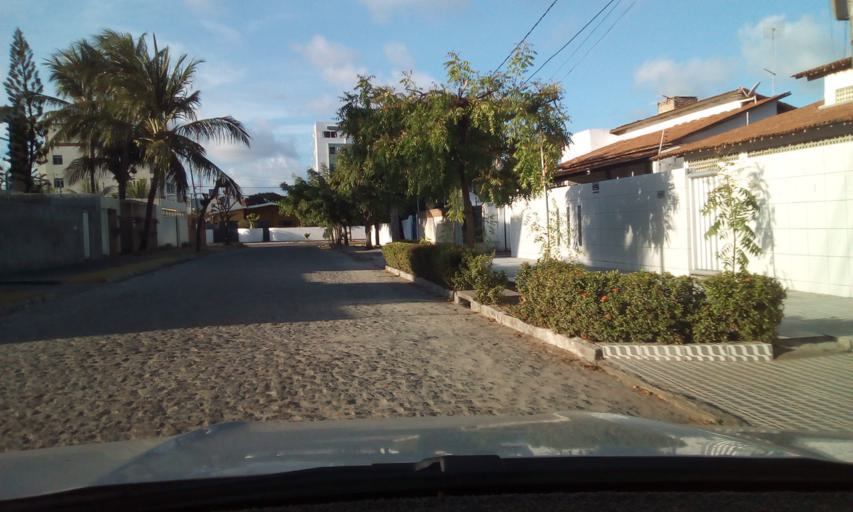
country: BR
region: Paraiba
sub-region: Joao Pessoa
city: Joao Pessoa
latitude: -7.0635
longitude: -34.8427
